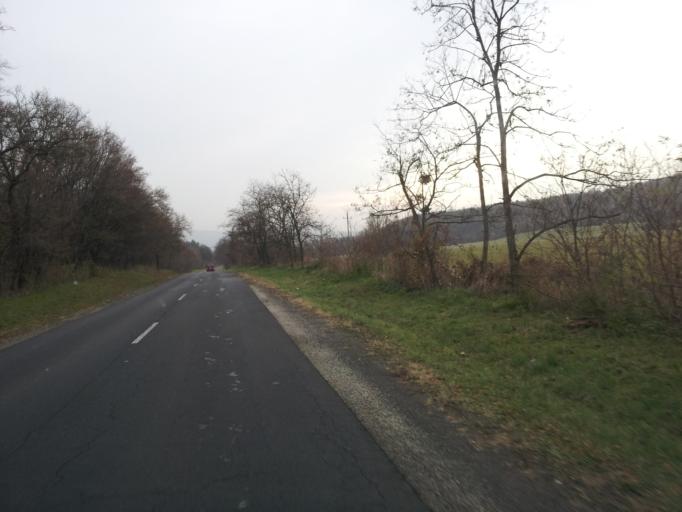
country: HU
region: Veszprem
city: Sumeg
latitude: 46.9173
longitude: 17.2466
